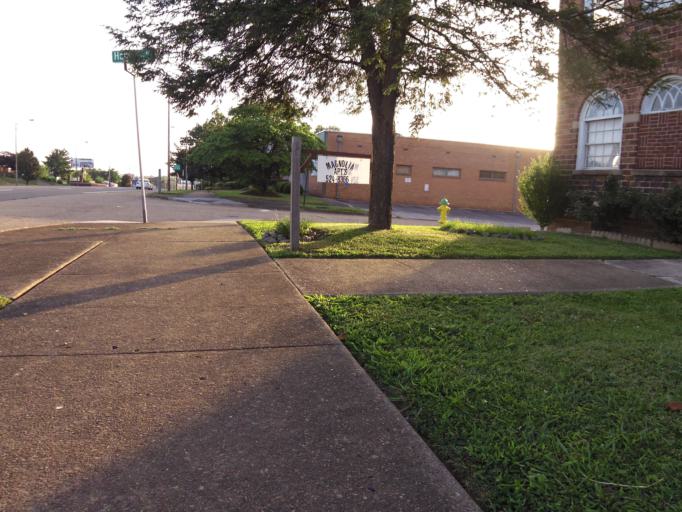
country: US
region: Tennessee
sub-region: Knox County
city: Knoxville
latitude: 35.9789
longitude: -83.9077
